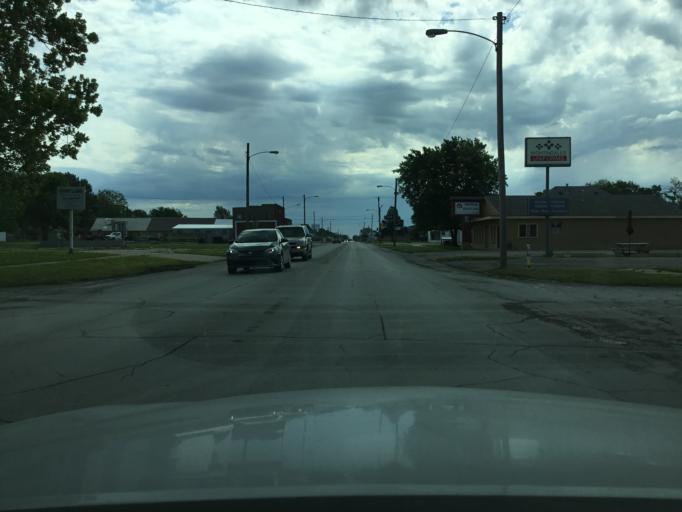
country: US
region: Kansas
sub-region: Montgomery County
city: Coffeyville
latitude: 37.0362
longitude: -95.6400
